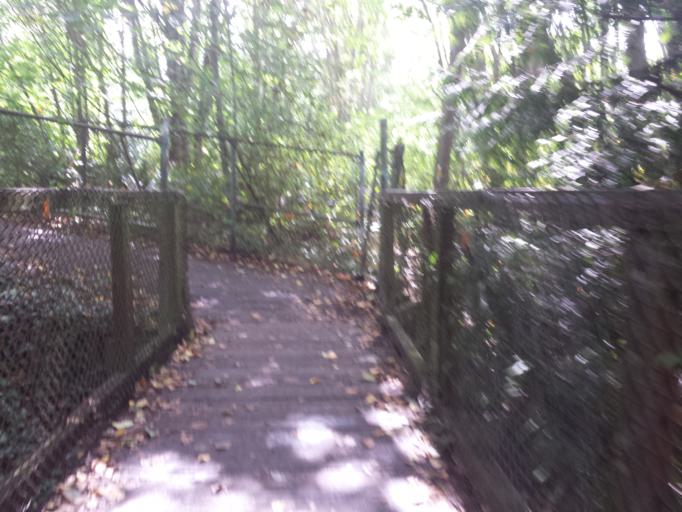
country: US
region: Washington
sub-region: King County
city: Seattle
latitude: 47.6633
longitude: -122.3996
